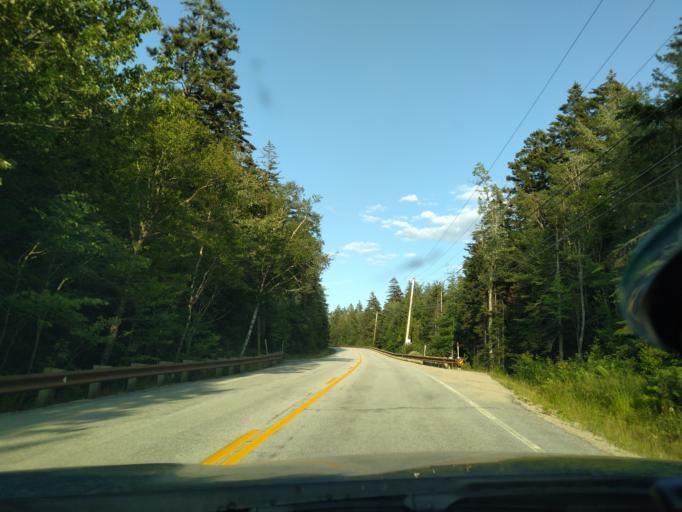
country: US
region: Maine
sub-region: Hancock County
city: Gouldsboro
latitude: 44.3936
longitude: -68.0709
